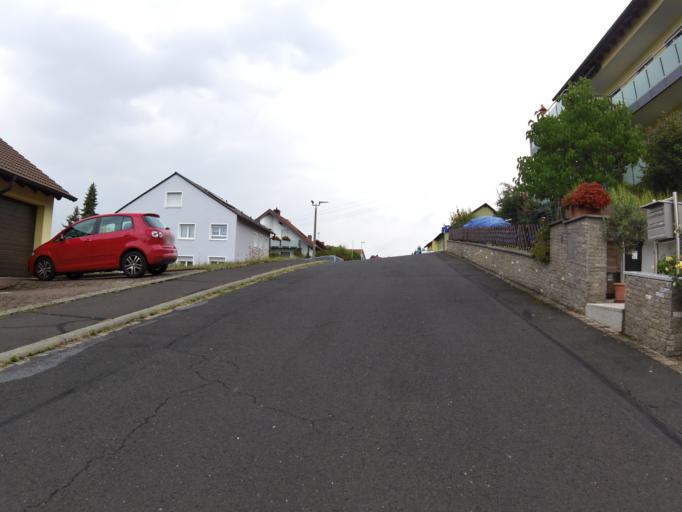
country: DE
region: Bavaria
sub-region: Regierungsbezirk Unterfranken
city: Guntersleben
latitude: 49.8729
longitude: 9.9101
